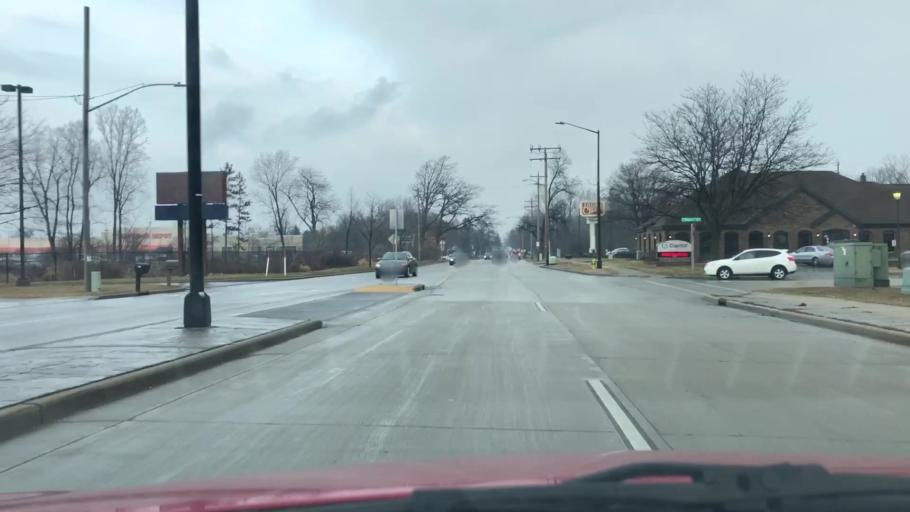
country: US
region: Wisconsin
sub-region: Brown County
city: Howard
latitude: 44.5248
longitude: -88.0789
